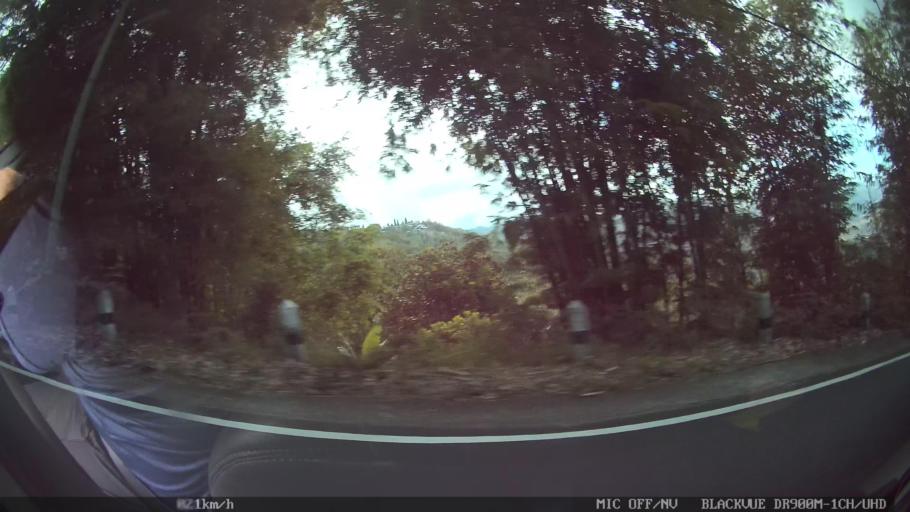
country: ID
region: Bali
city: Banjar Kedisan
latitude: -8.2599
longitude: 115.3402
